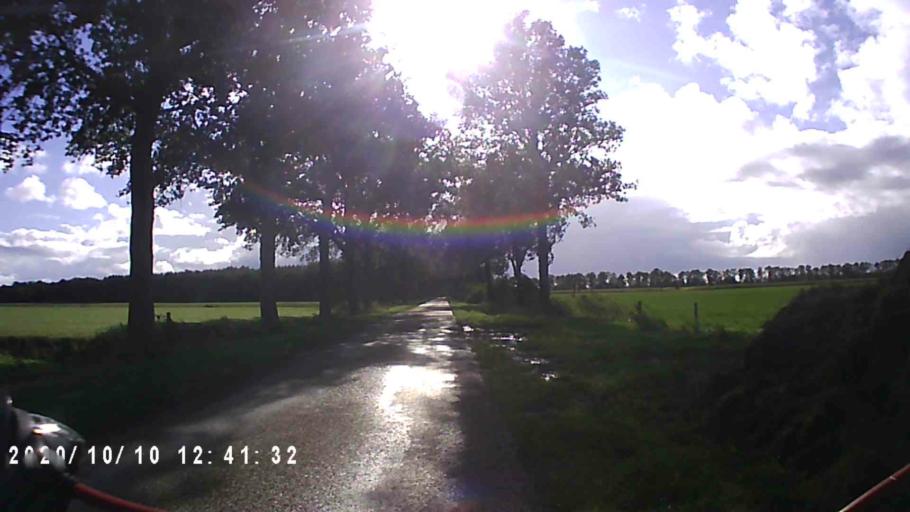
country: NL
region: Friesland
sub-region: Gemeente Weststellingwerf
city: Noordwolde
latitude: 52.9382
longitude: 6.2171
